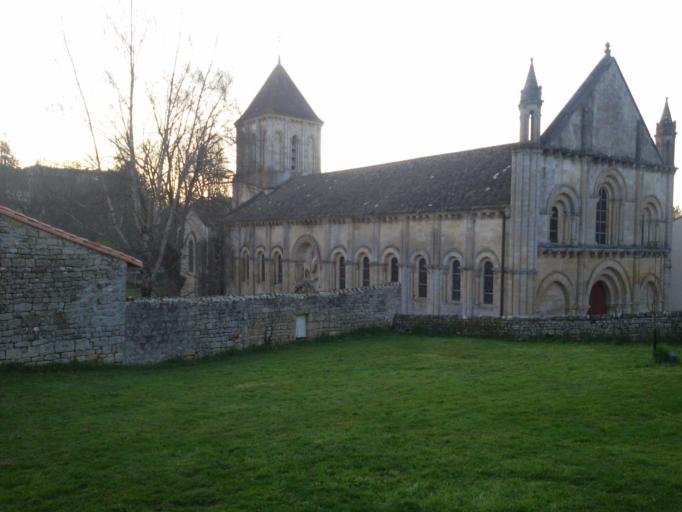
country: FR
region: Poitou-Charentes
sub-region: Departement des Deux-Sevres
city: Melle
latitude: 46.2202
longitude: -0.1504
